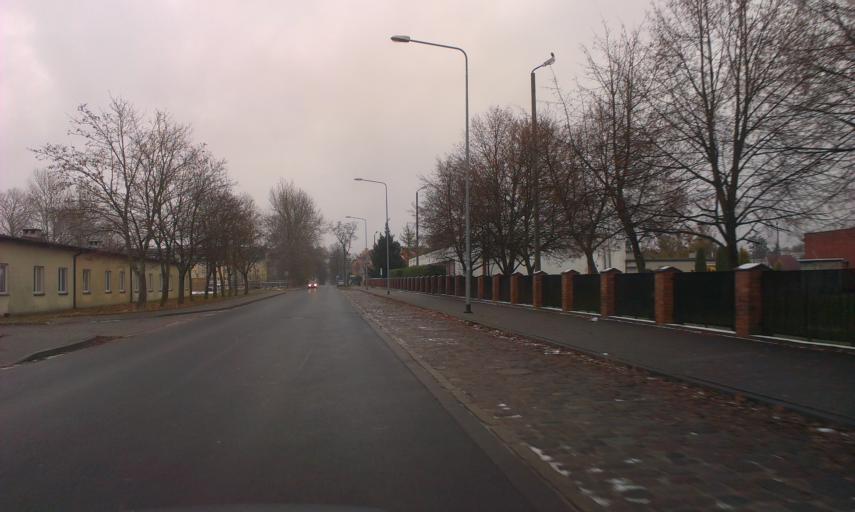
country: PL
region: West Pomeranian Voivodeship
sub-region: Powiat szczecinecki
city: Szczecinek
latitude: 53.7194
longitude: 16.6729
